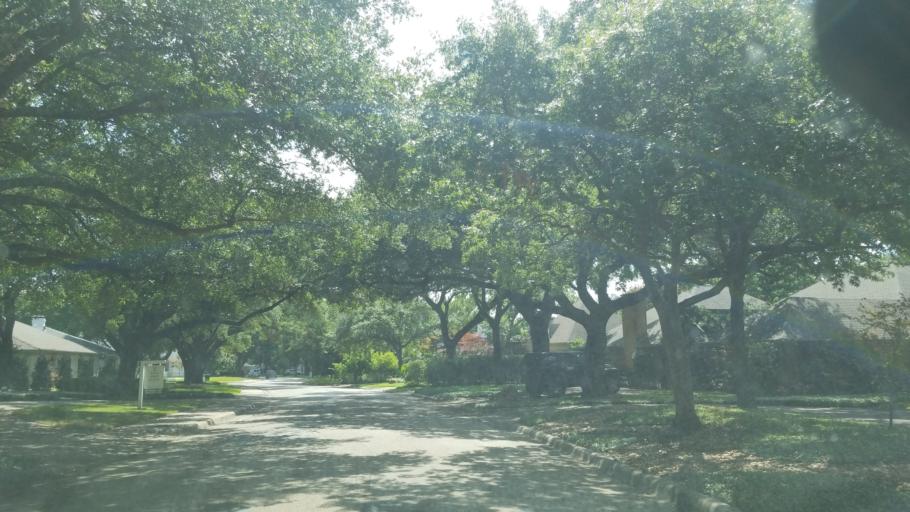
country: US
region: Texas
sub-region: Dallas County
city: University Park
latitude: 32.8312
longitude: -96.8203
